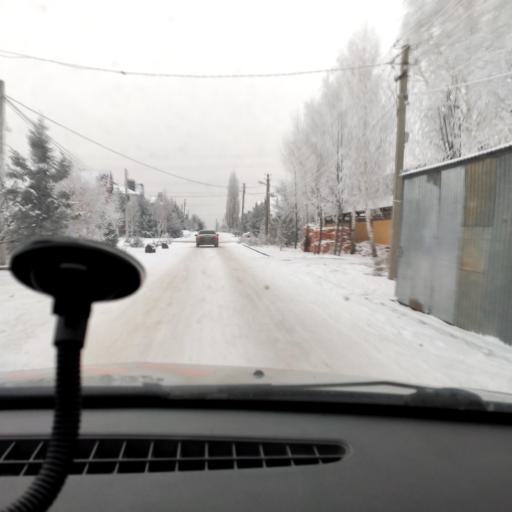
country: RU
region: Bashkortostan
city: Ufa
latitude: 54.5997
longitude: 55.9324
